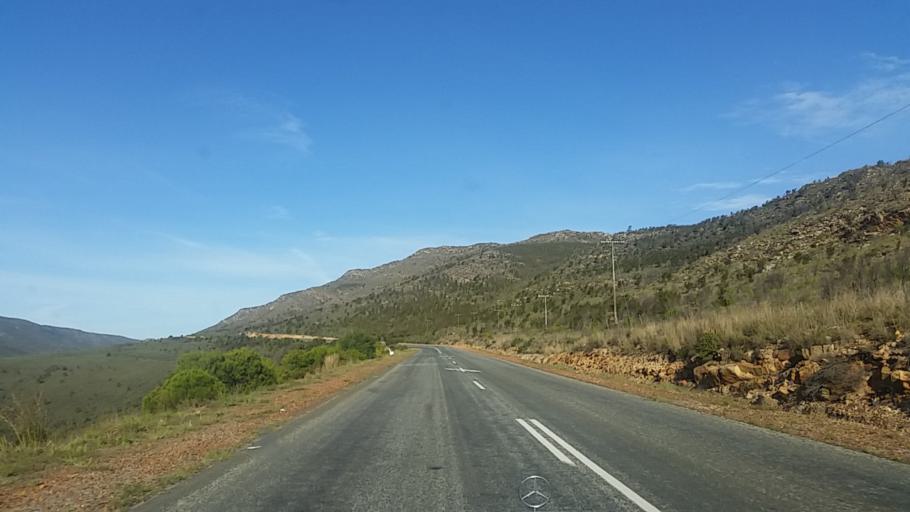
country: ZA
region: Western Cape
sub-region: Eden District Municipality
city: Knysna
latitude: -33.7521
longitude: 22.9535
